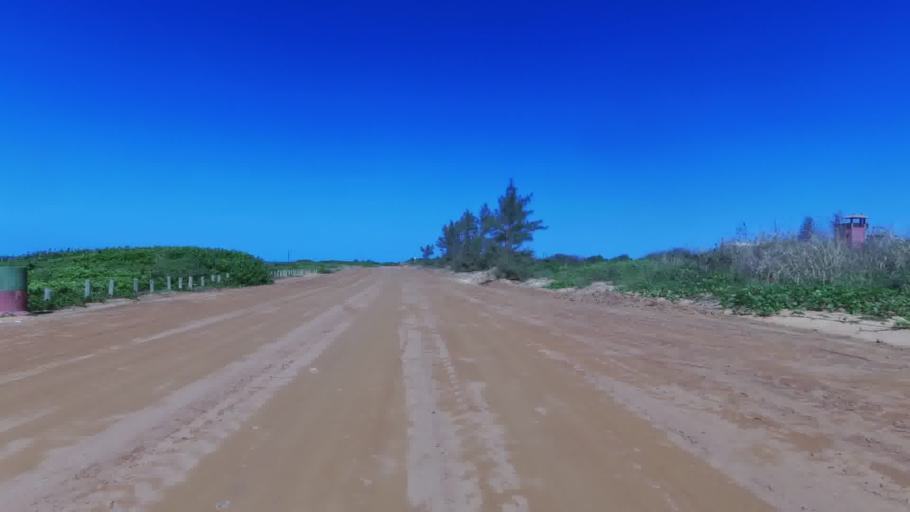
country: BR
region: Espirito Santo
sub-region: Piuma
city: Piuma
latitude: -20.8379
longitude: -40.6276
